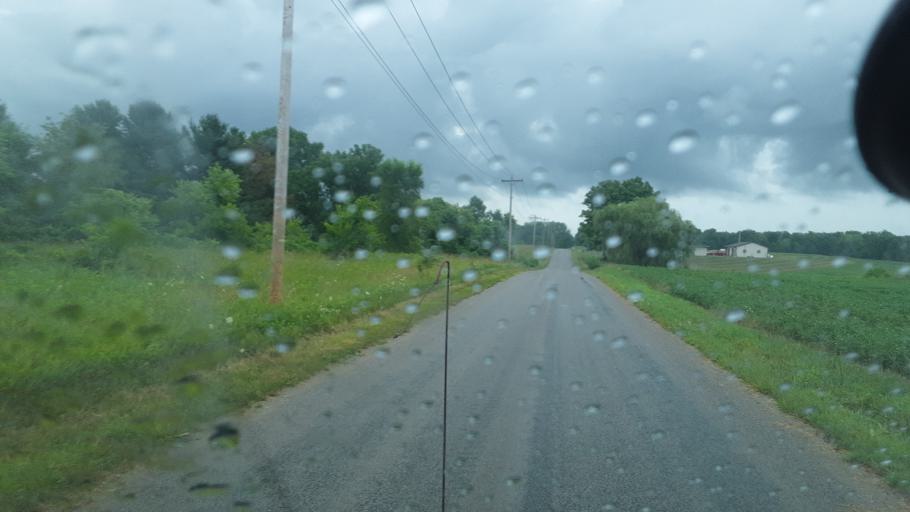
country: US
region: Indiana
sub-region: Steuben County
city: Hamilton
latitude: 41.5402
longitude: -84.8539
